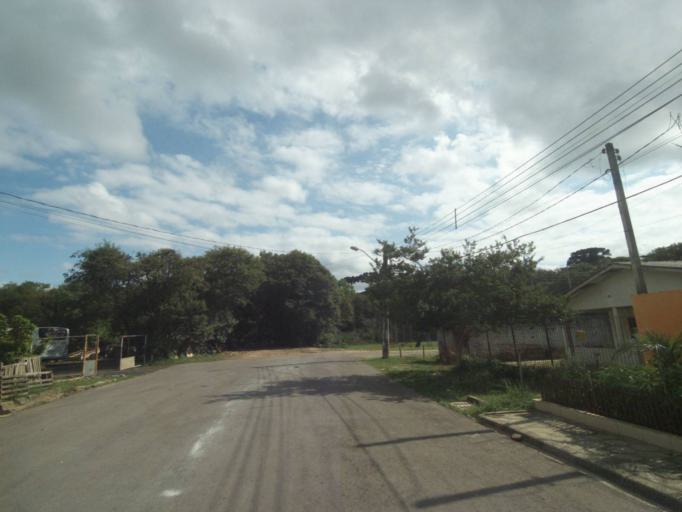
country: BR
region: Parana
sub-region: Curitiba
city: Curitiba
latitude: -25.3826
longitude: -49.3014
